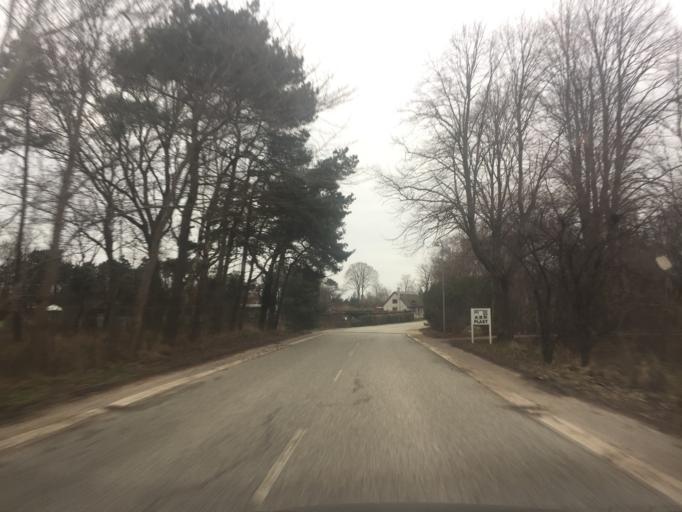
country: DK
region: Capital Region
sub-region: Halsnaes Kommune
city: Liseleje
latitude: 56.0004
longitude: 11.9748
